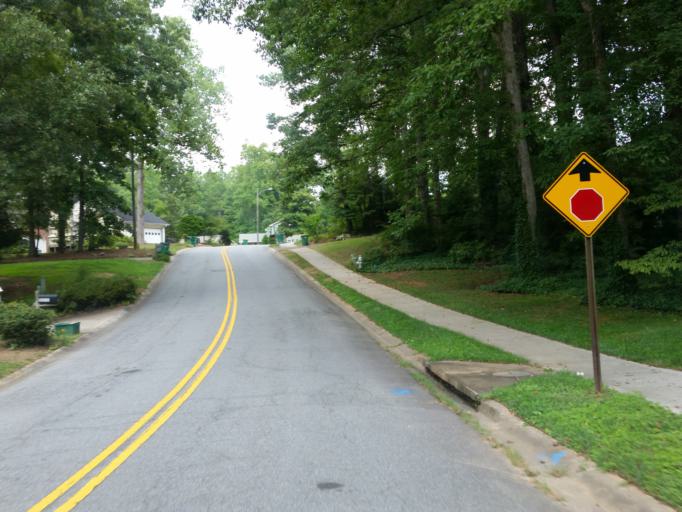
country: US
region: Georgia
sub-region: Fulton County
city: Sandy Springs
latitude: 33.9594
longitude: -84.4536
